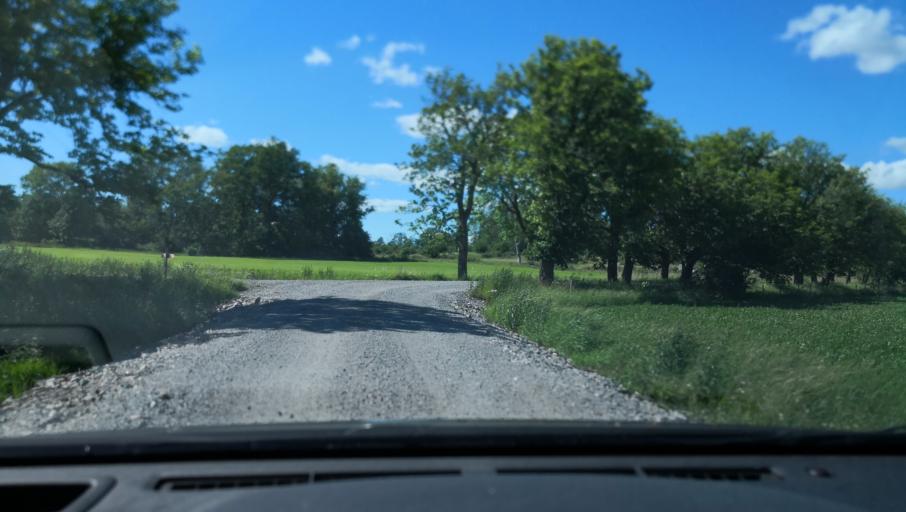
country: SE
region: Soedermanland
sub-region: Eskilstuna Kommun
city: Hallbybrunn
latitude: 59.2994
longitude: 16.3622
